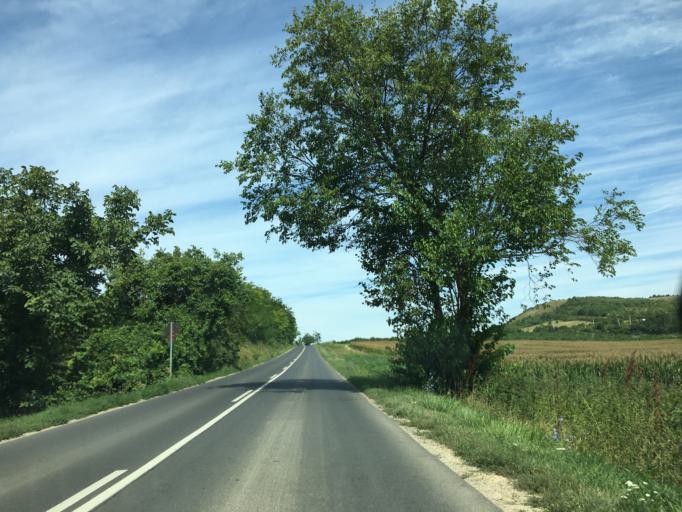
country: HU
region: Fejer
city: Many
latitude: 47.5778
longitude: 18.6748
